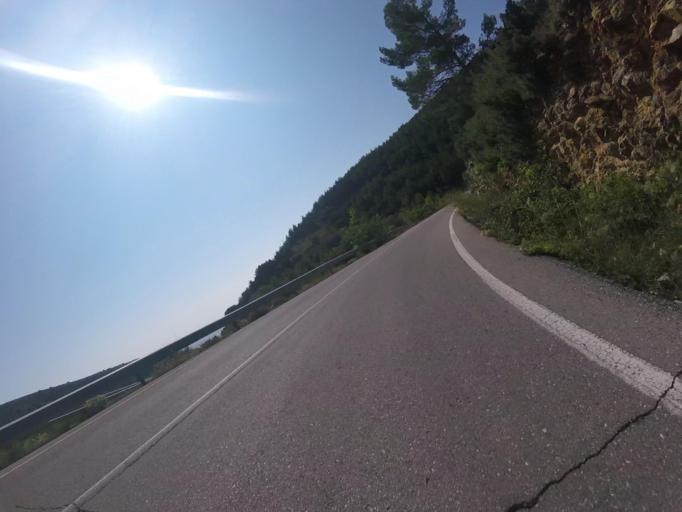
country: ES
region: Valencia
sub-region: Provincia de Castello
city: Benafigos
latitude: 40.2679
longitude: -0.2372
